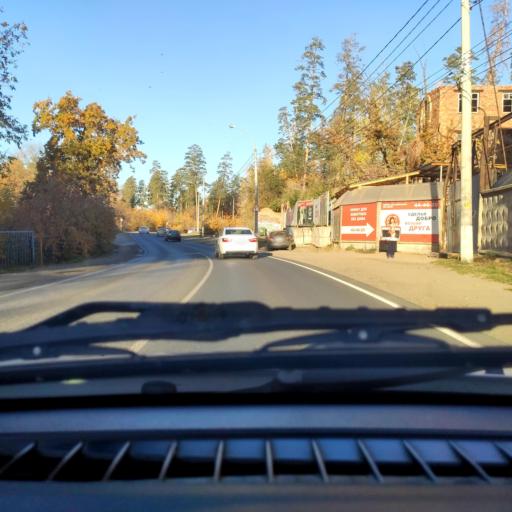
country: RU
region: Samara
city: Tol'yatti
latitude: 53.4884
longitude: 49.3099
